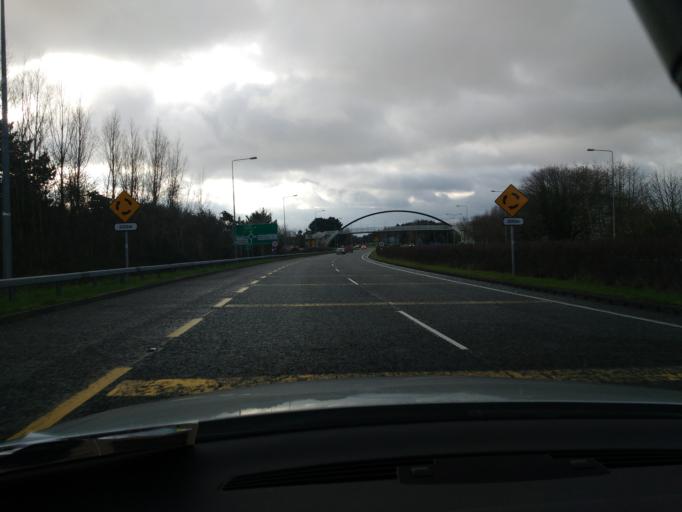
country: IE
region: Munster
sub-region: An Clar
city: Shannon
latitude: 52.7048
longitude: -8.8913
